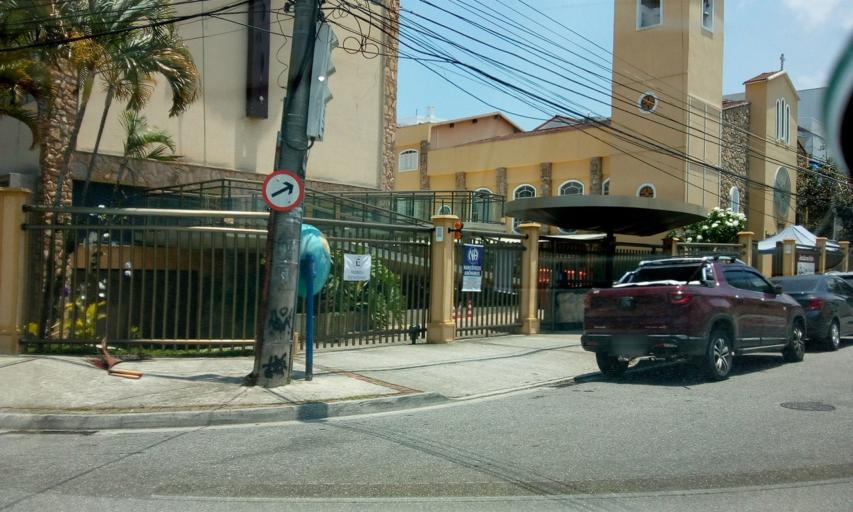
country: BR
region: Rio de Janeiro
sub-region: Nilopolis
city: Nilopolis
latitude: -23.0185
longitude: -43.4612
